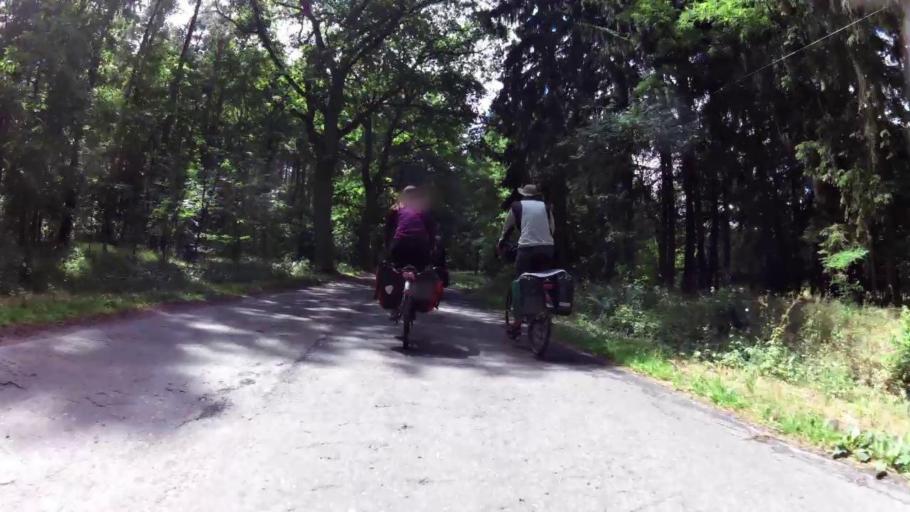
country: PL
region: West Pomeranian Voivodeship
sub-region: Powiat lobeski
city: Resko
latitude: 53.7575
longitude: 15.5165
